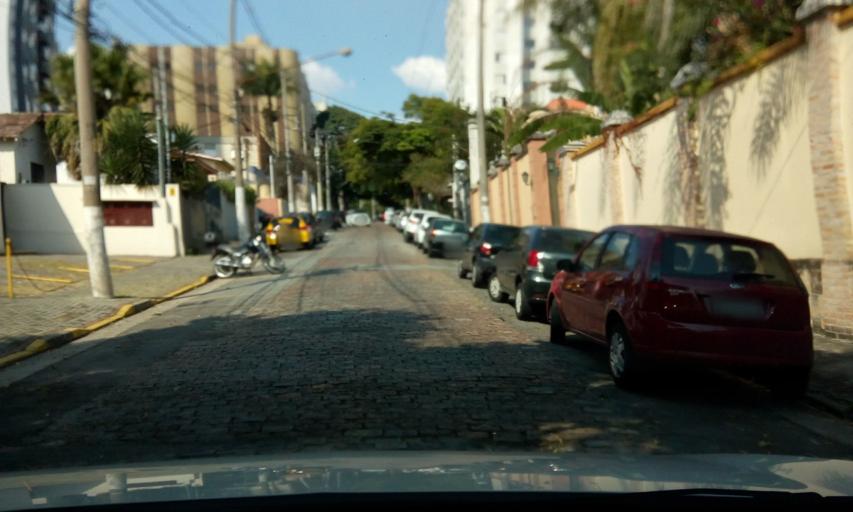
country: BR
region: Sao Paulo
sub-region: Sao Paulo
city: Sao Paulo
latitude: -23.6053
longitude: -46.6775
